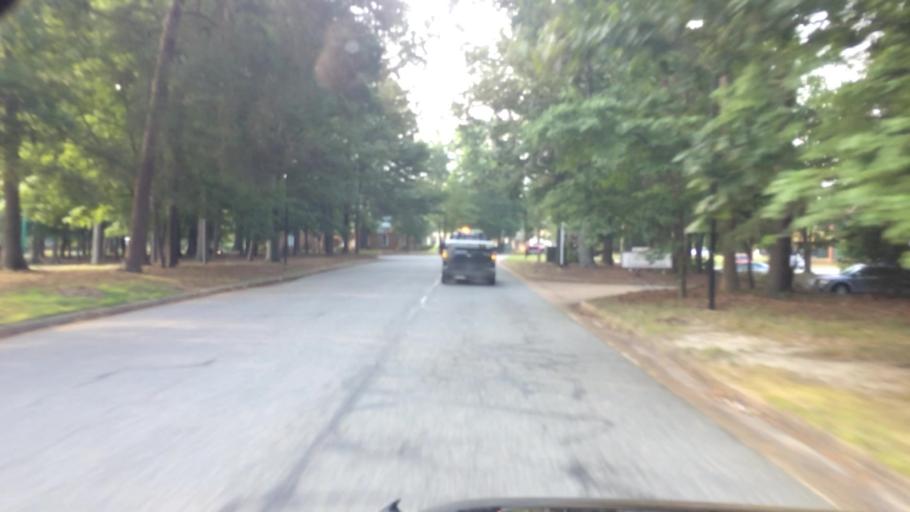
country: US
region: Virginia
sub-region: City of Williamsburg
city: Williamsburg
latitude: 37.2463
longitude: -76.6601
